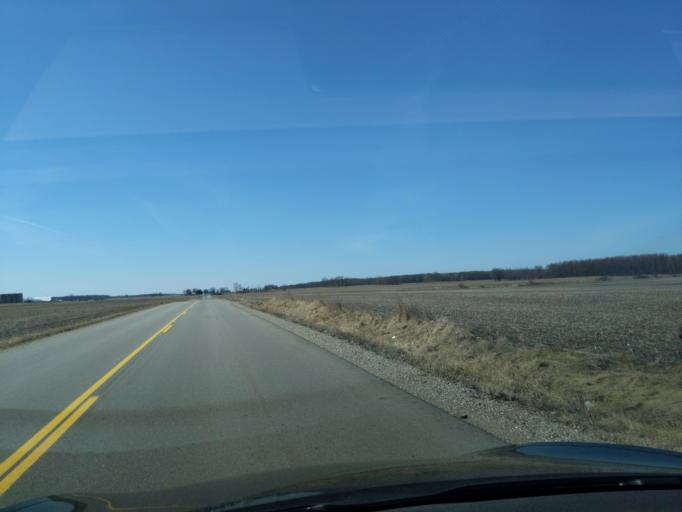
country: US
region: Michigan
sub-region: Eaton County
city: Grand Ledge
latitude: 42.7266
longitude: -84.8627
